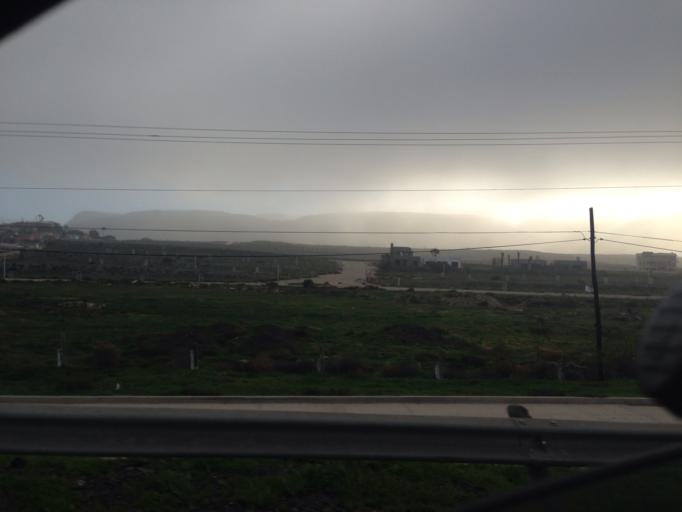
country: MX
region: Baja California
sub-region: Playas de Rosarito
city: Santa Anita
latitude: 32.0843
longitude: -116.8824
